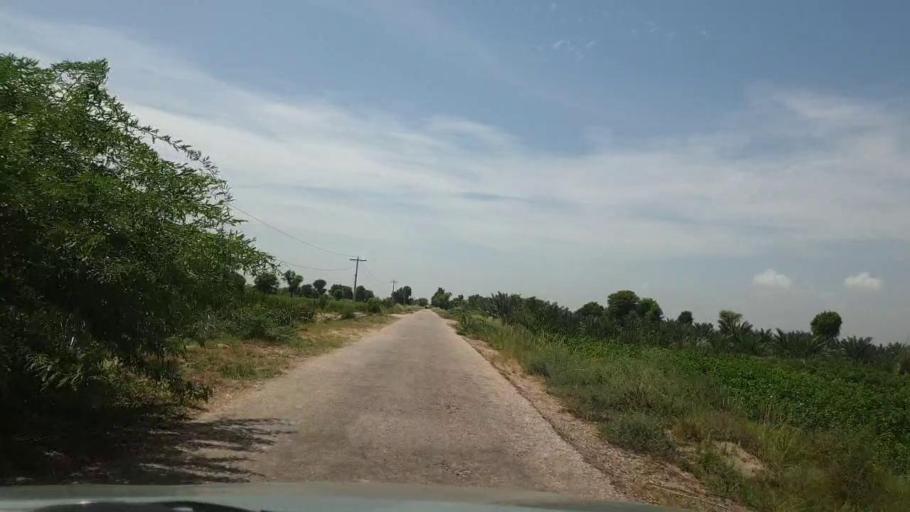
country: PK
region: Sindh
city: Bozdar
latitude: 27.0573
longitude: 68.9811
